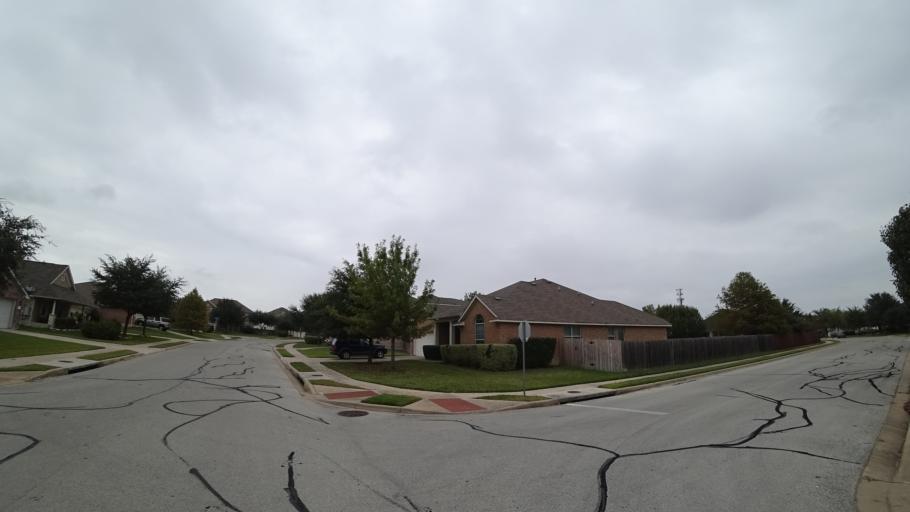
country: US
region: Texas
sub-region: Travis County
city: Pflugerville
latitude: 30.4270
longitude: -97.6189
